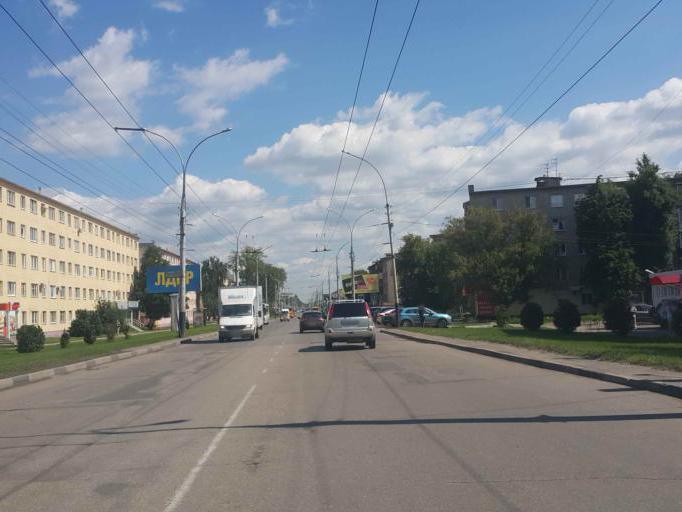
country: RU
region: Tambov
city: Tambov
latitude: 52.7437
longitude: 41.4522
